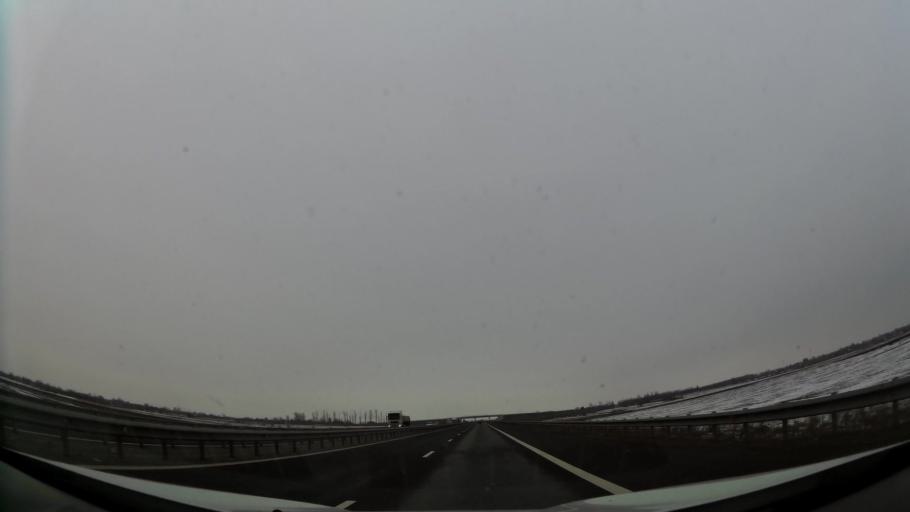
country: RO
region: Ilfov
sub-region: Comuna Gruiu
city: Gruiu
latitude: 44.7130
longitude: 26.2383
